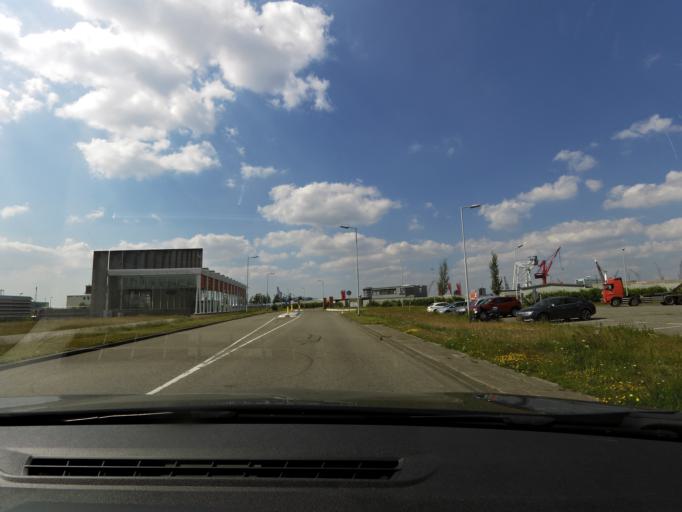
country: NL
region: South Holland
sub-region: Gemeente Schiedam
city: Schiedam
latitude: 51.8950
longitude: 4.3768
